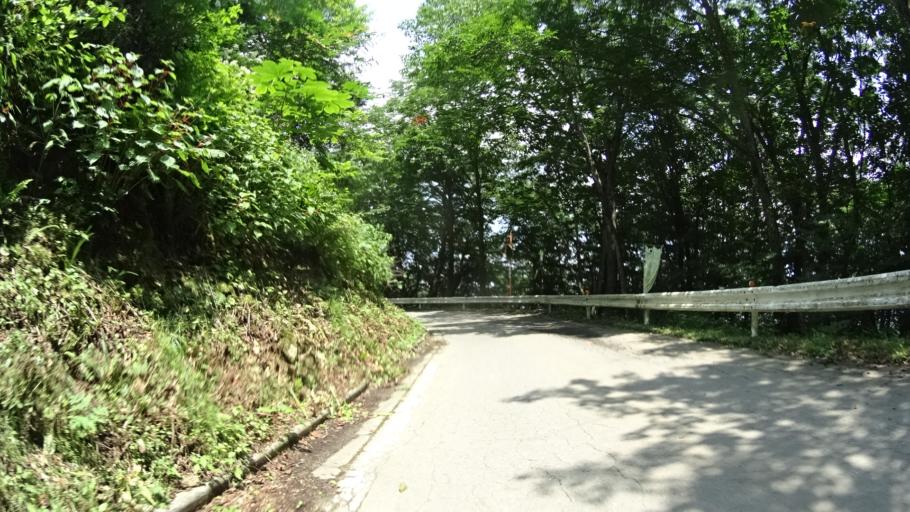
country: JP
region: Nagano
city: Saku
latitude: 36.1009
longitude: 138.6506
